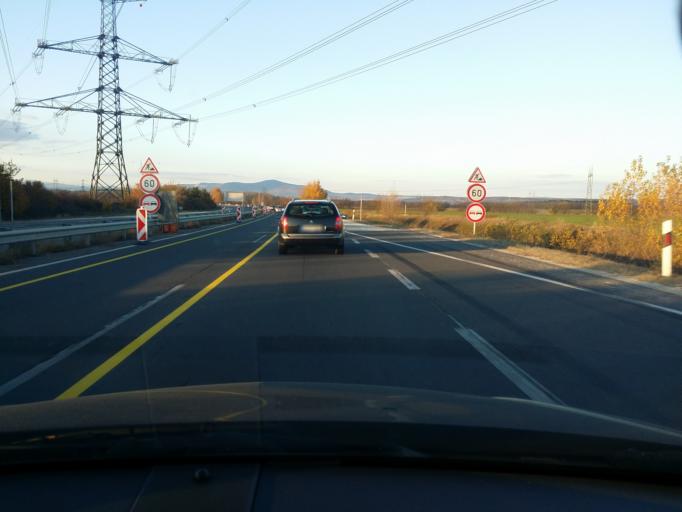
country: HU
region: Pest
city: Szod
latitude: 47.6861
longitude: 19.1748
